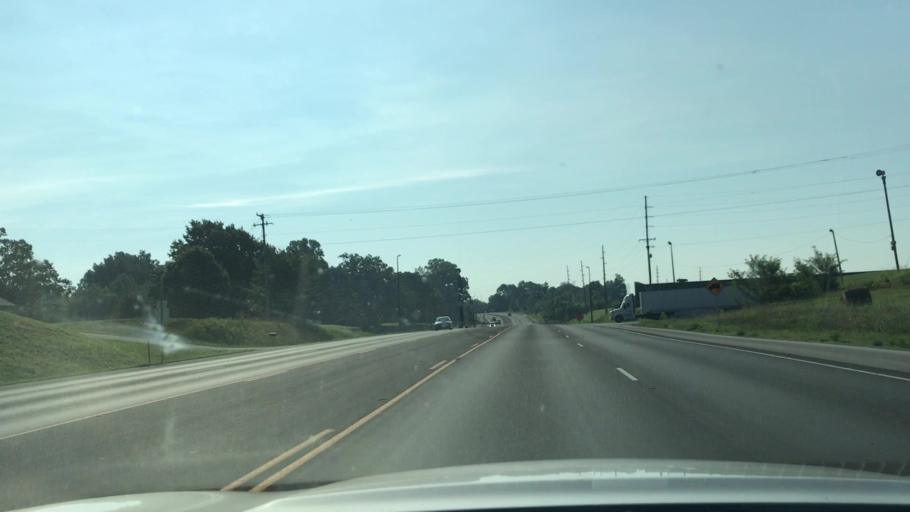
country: US
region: Kentucky
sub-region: Barren County
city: Glasgow
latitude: 37.0115
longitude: -85.9514
